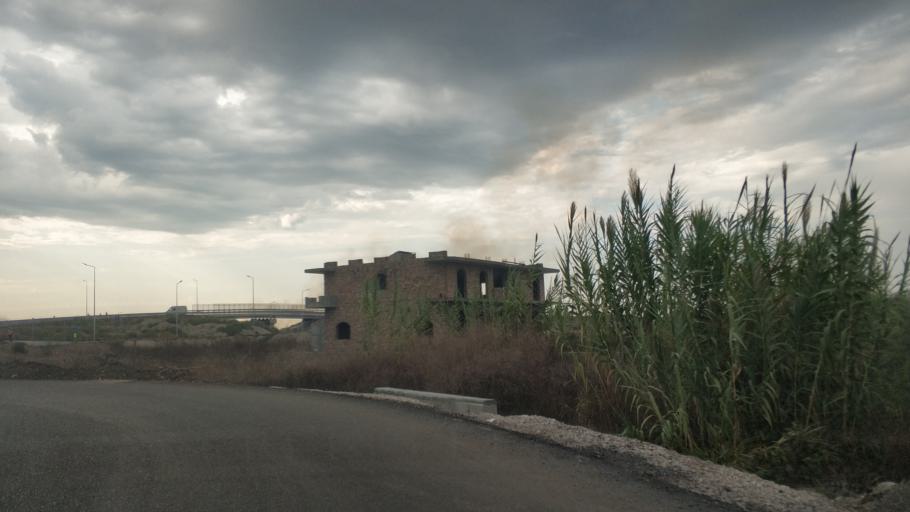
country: AL
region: Fier
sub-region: Rrethi i Fierit
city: Mbrostar-Ure
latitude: 40.7467
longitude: 19.5595
